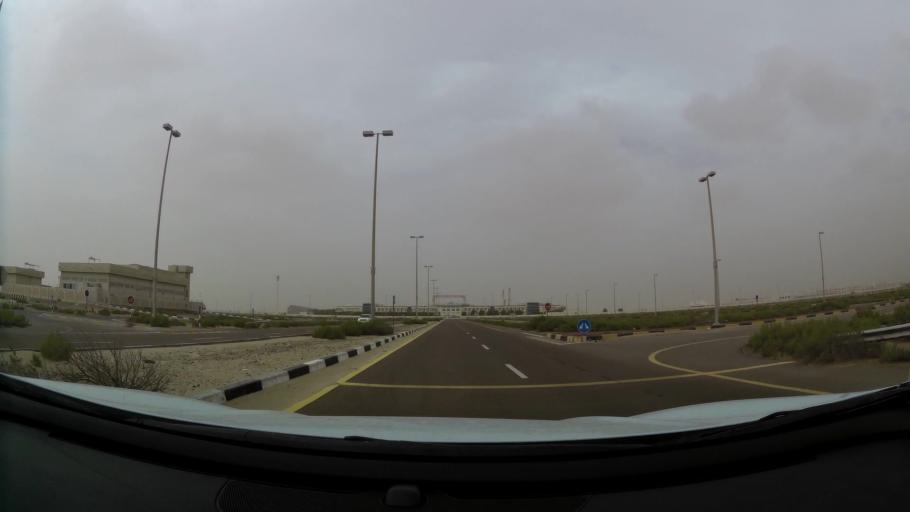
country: AE
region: Abu Dhabi
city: Abu Dhabi
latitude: 24.3693
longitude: 54.6880
